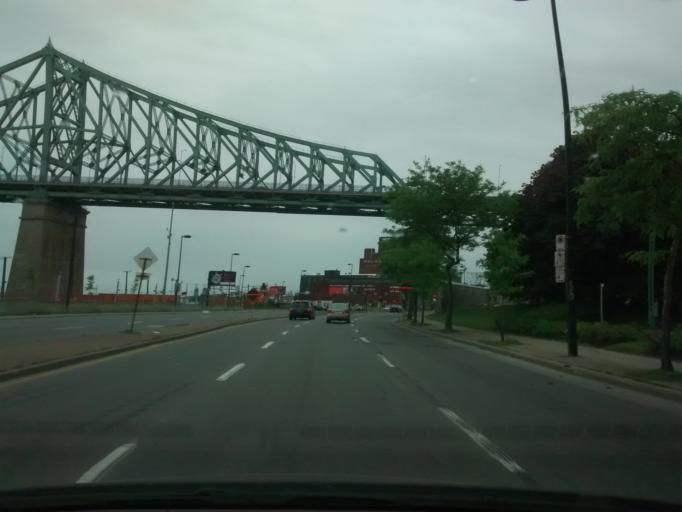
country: CA
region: Quebec
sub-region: Monteregie
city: Longueuil
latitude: 45.5244
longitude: -73.5456
